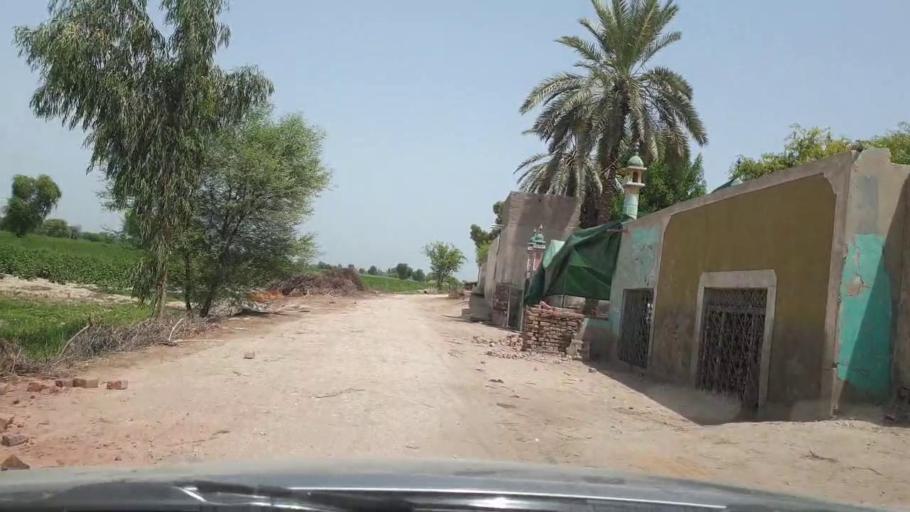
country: PK
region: Sindh
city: Pano Aqil
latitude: 27.8321
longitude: 69.1908
